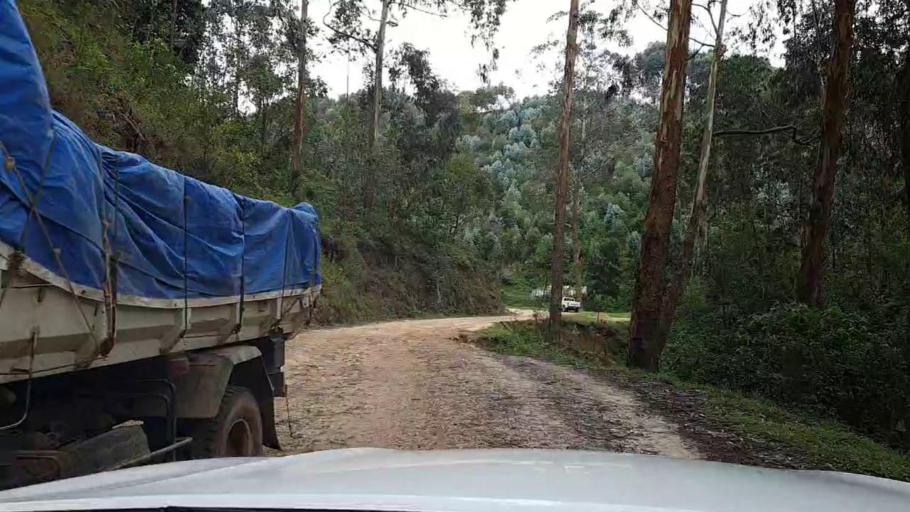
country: RW
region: Western Province
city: Kibuye
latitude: -2.2690
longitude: 29.3619
